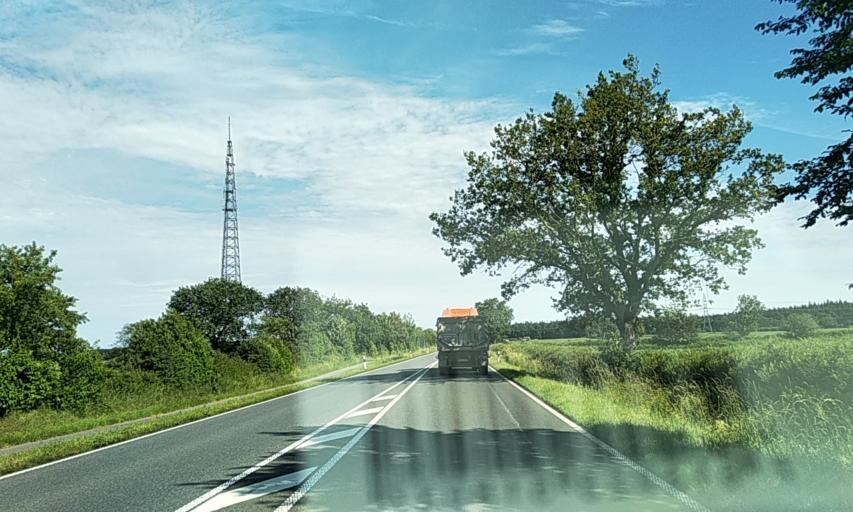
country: DE
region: Schleswig-Holstein
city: Lohe-Fohrden
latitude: 54.3662
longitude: 9.5509
